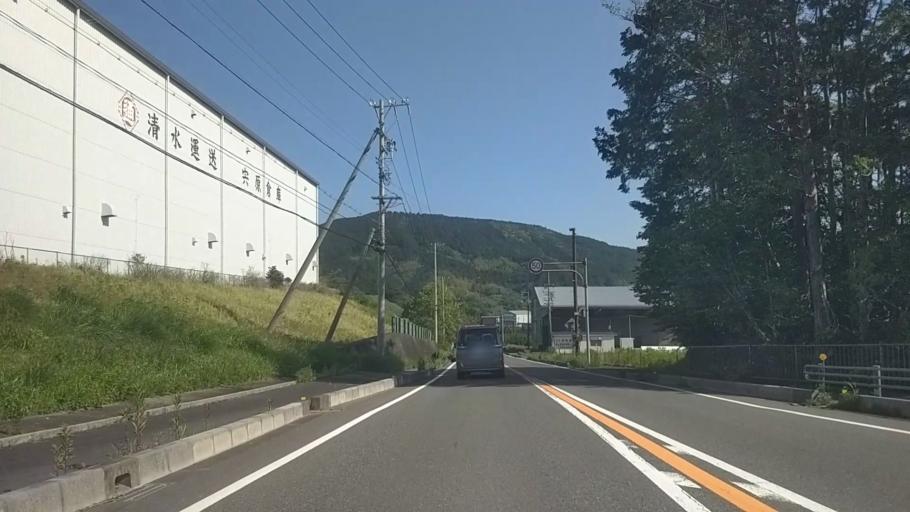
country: JP
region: Shizuoka
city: Fujinomiya
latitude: 35.1540
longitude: 138.5204
